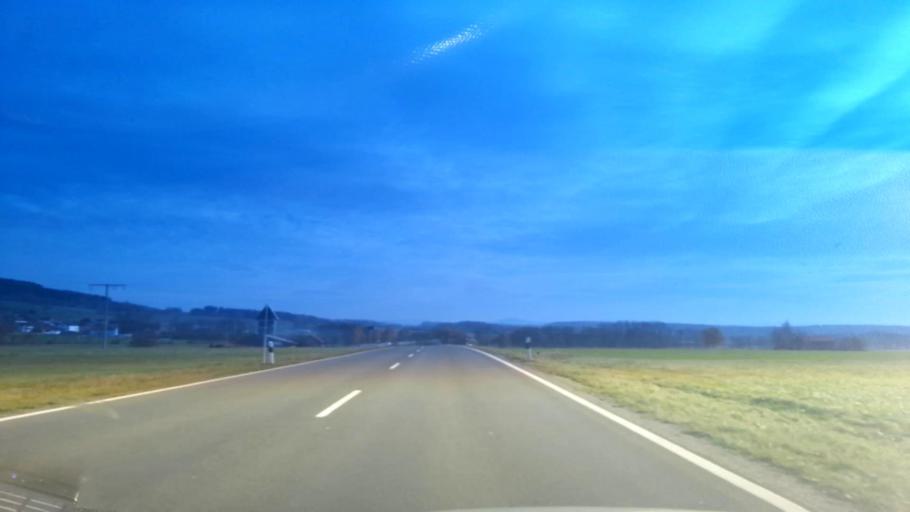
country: DE
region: Bavaria
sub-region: Upper Franconia
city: Kirchenpingarten
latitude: 49.9211
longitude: 11.8111
